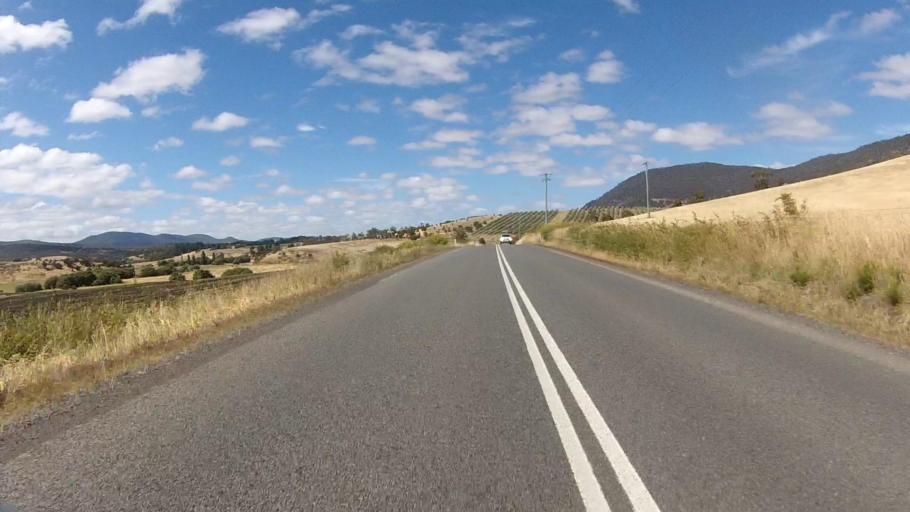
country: AU
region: Tasmania
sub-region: Brighton
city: Old Beach
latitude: -42.5995
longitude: 147.4160
